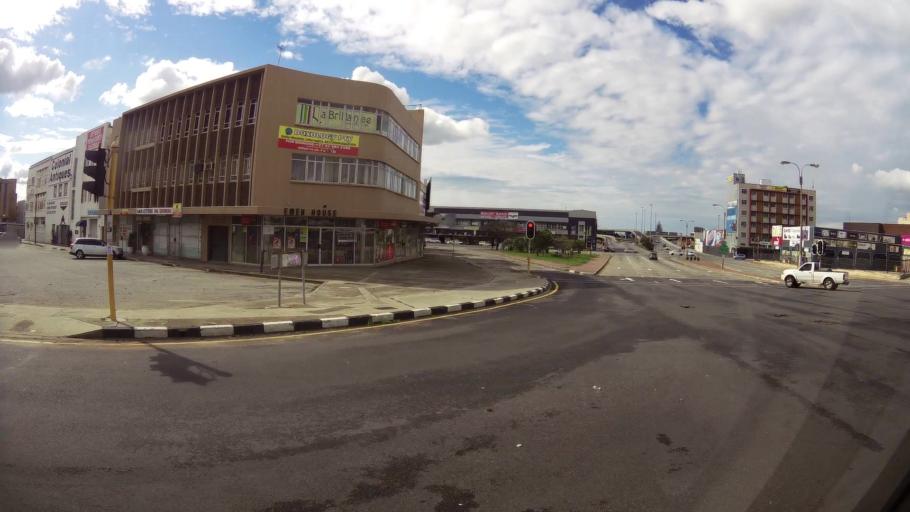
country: ZA
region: Eastern Cape
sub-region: Nelson Mandela Bay Metropolitan Municipality
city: Port Elizabeth
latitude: -33.9466
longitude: 25.6049
